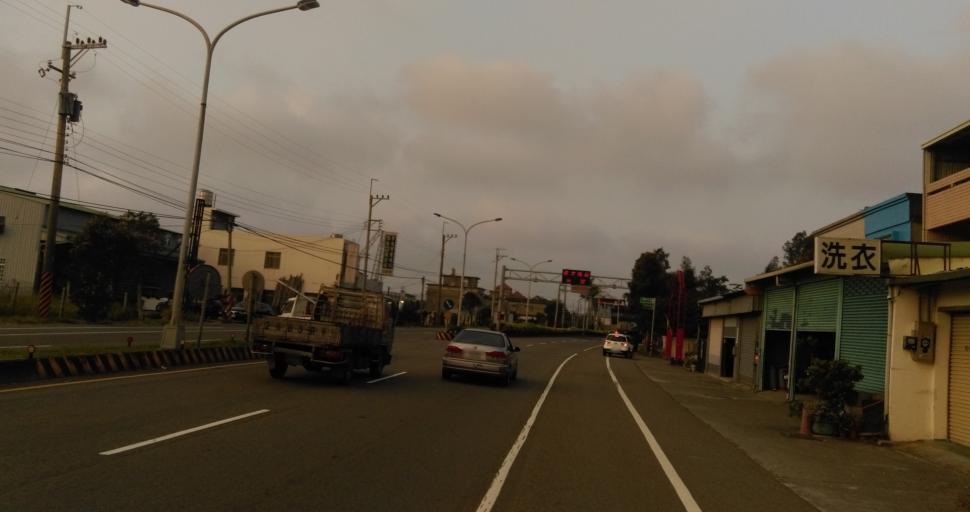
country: TW
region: Taiwan
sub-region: Hsinchu
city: Hsinchu
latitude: 24.8169
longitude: 120.9235
